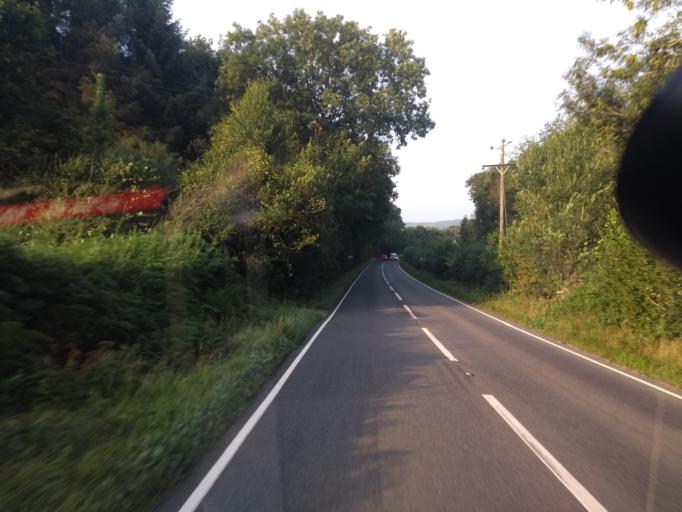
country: GB
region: England
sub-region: Somerset
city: Chard
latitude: 50.9014
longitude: -3.0456
